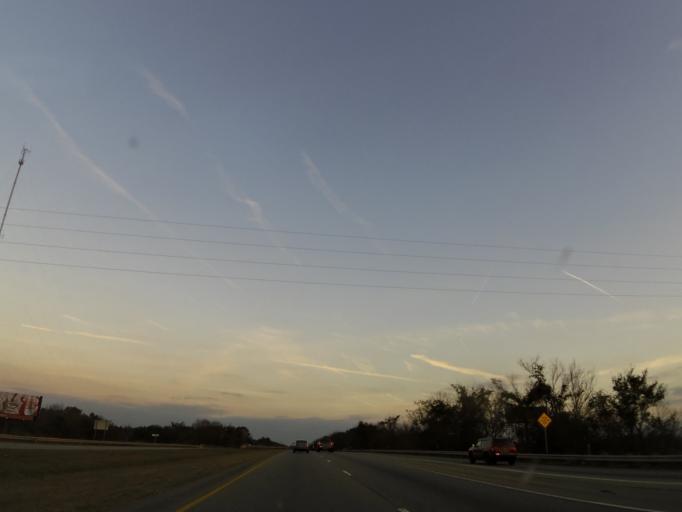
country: US
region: Georgia
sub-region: Dougherty County
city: Albany
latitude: 31.6039
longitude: -84.1510
